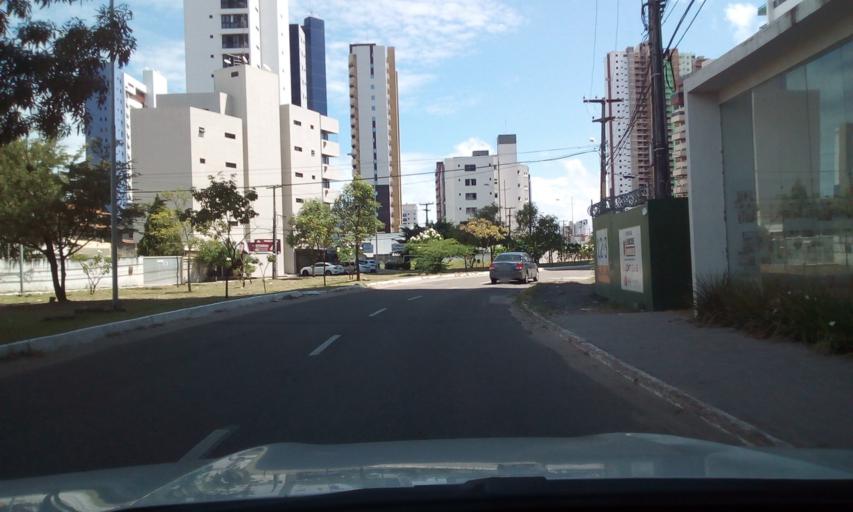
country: BR
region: Paraiba
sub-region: Joao Pessoa
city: Joao Pessoa
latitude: -7.0816
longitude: -34.8396
